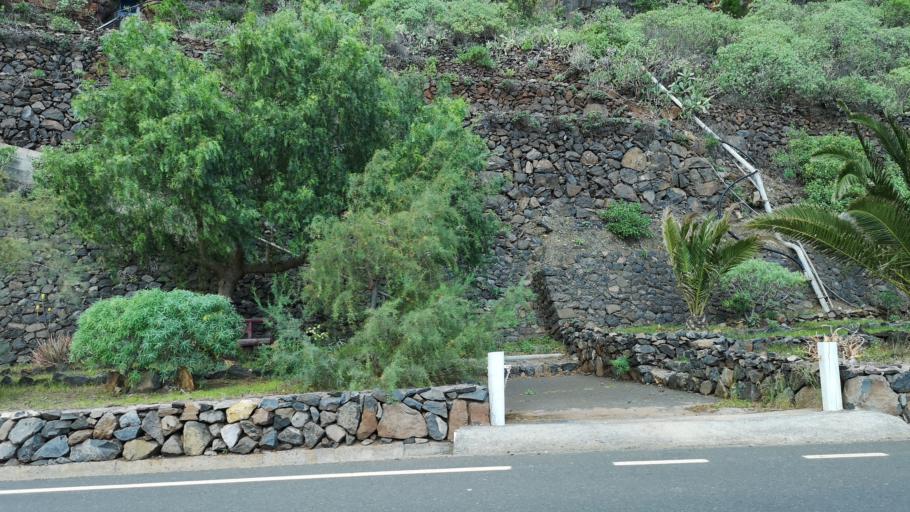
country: ES
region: Canary Islands
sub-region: Provincia de Santa Cruz de Tenerife
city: Agulo
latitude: 28.1906
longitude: -17.1980
